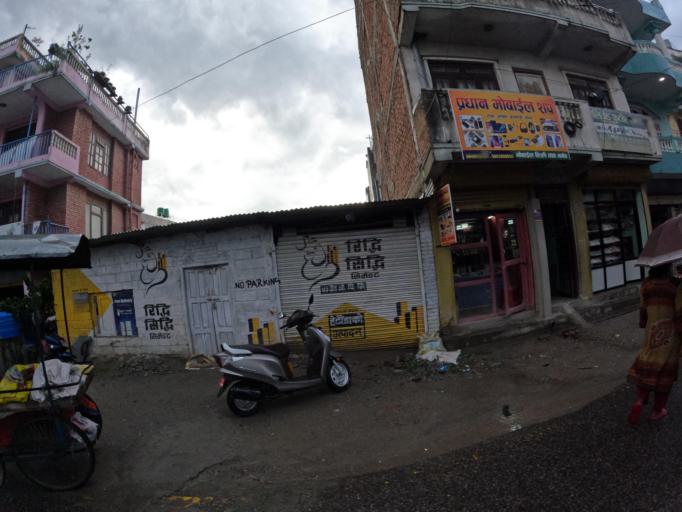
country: NP
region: Central Region
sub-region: Bagmati Zone
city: Kathmandu
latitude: 27.7654
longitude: 85.3305
